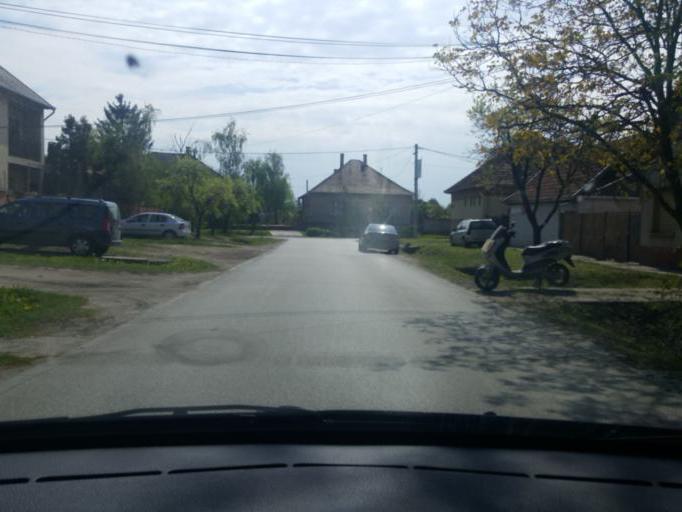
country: HU
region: Pest
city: Monor
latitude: 47.3460
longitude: 19.4463
